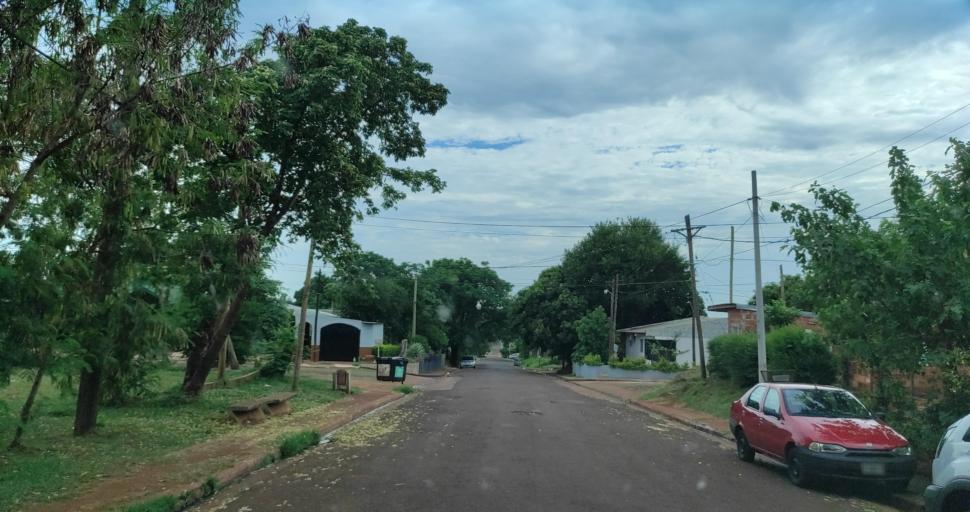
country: AR
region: Misiones
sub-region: Departamento de Capital
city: Posadas
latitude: -27.3898
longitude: -55.9301
